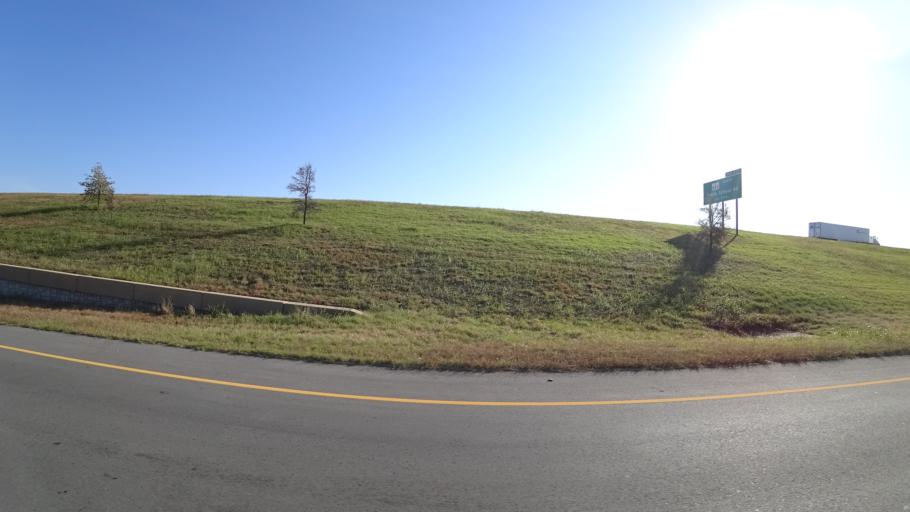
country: US
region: Texas
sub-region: Williamson County
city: Hutto
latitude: 30.5357
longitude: -97.5771
